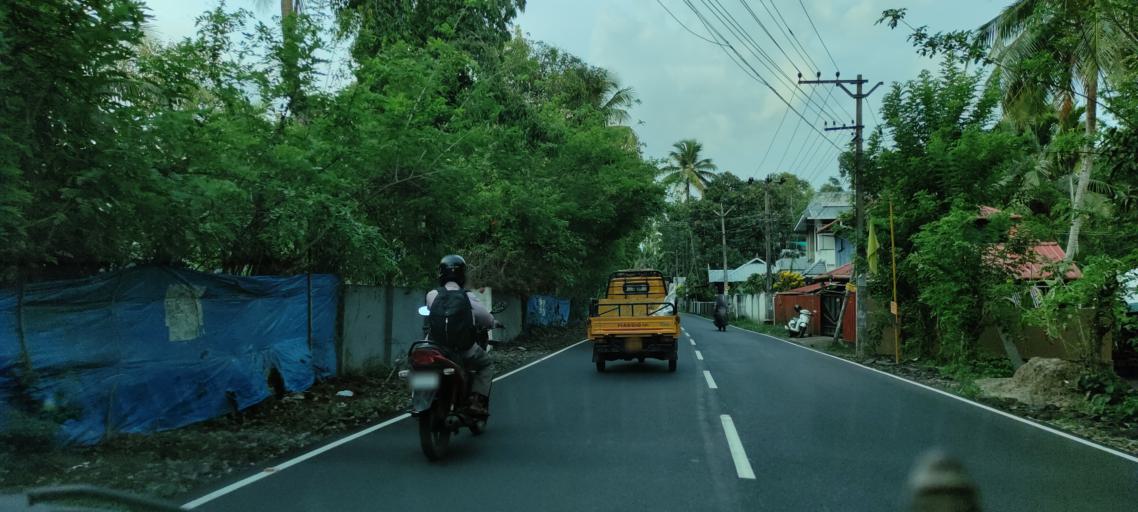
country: IN
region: Kerala
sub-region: Alappuzha
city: Kutiatodu
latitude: 9.8290
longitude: 76.3416
